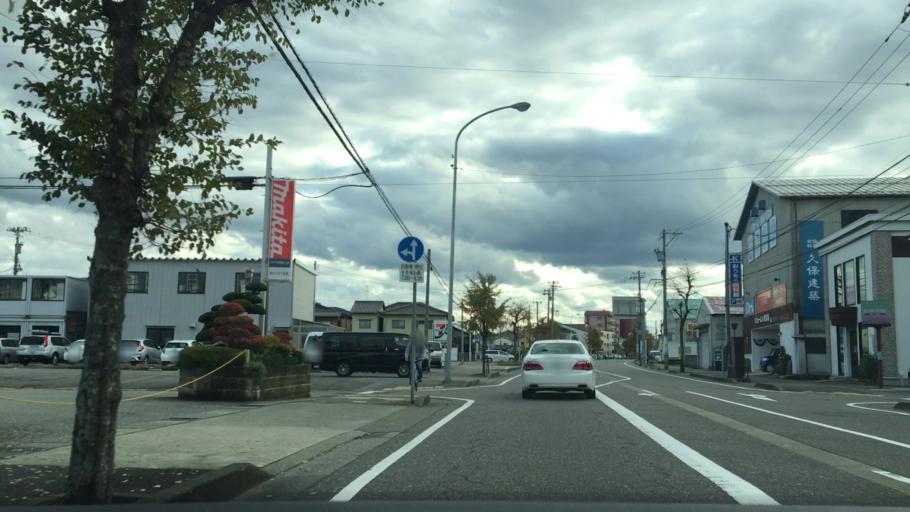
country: JP
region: Ishikawa
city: Nonoichi
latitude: 36.5264
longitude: 136.6187
